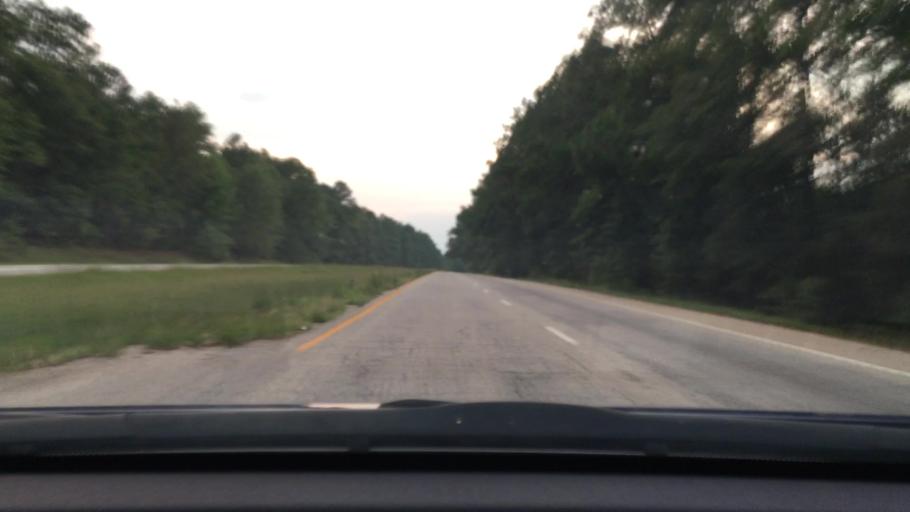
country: US
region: South Carolina
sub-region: Sumter County
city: Stateburg
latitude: 33.9458
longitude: -80.5300
